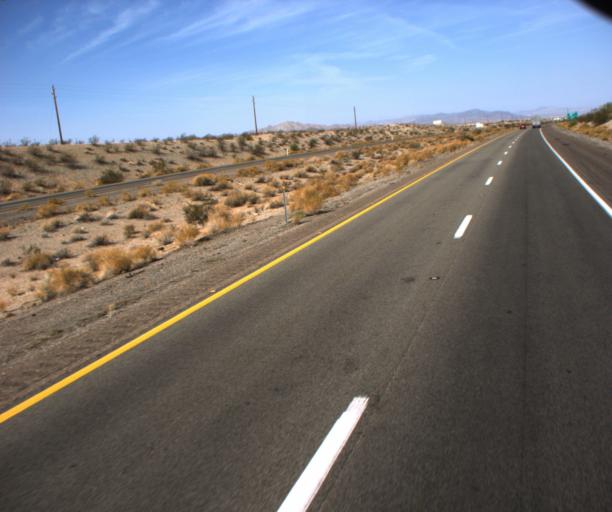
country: US
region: Arizona
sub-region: Mohave County
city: Desert Hills
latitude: 34.7313
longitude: -114.2741
